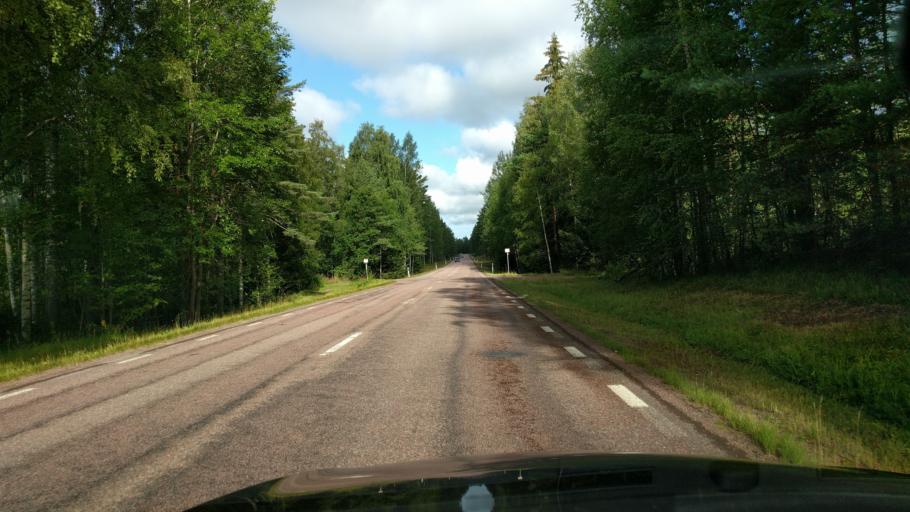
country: SE
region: Dalarna
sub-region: Mora Kommun
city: Mora
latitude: 61.0656
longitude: 14.3913
